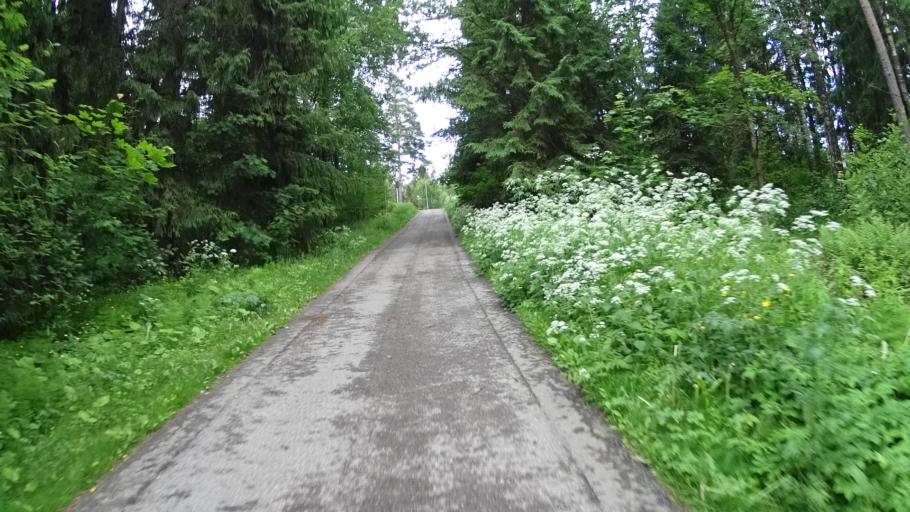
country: FI
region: Uusimaa
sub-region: Helsinki
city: Kilo
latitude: 60.2725
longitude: 24.8214
